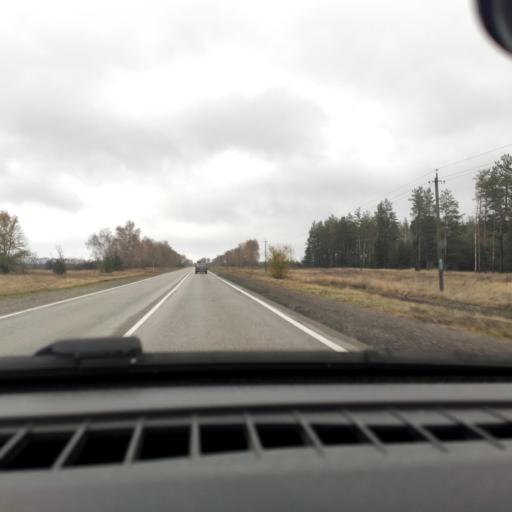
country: RU
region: Voronezj
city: Uryv-Pokrovka
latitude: 51.0584
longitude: 38.9904
